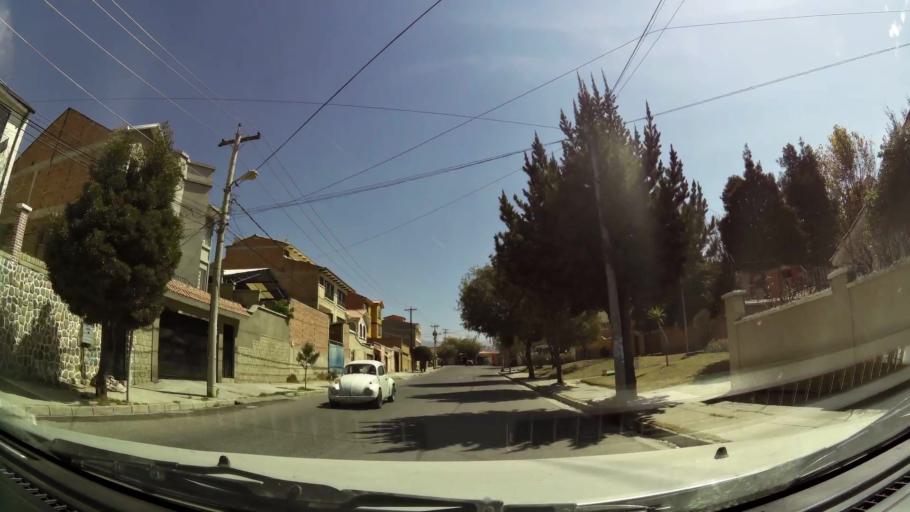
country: BO
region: La Paz
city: La Paz
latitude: -16.5340
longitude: -68.1029
